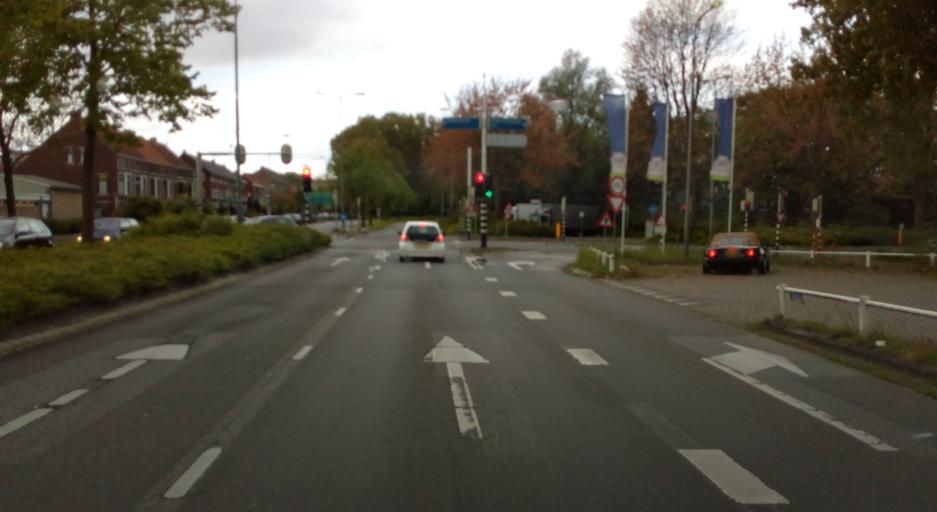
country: NL
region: South Holland
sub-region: Gemeente Dordrecht
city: Dordrecht
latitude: 51.8050
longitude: 4.6553
